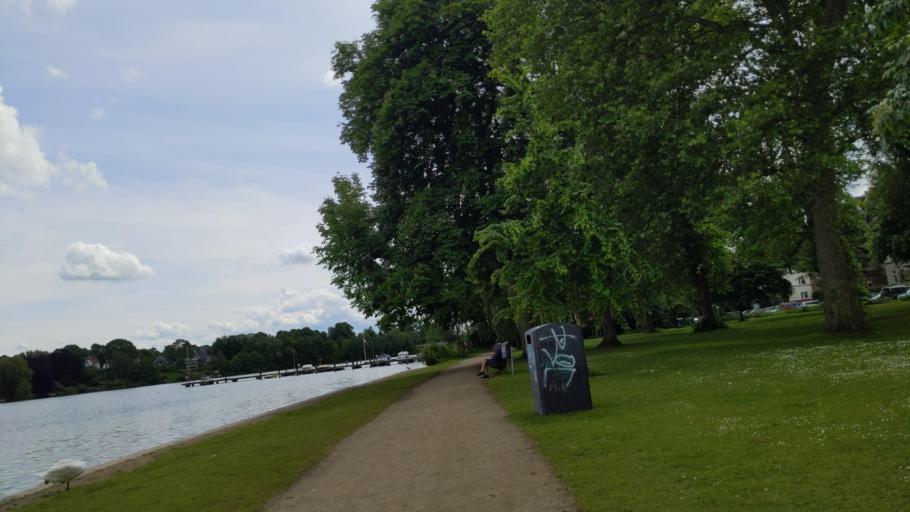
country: DE
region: Schleswig-Holstein
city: Luebeck
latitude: 53.8679
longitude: 10.7047
